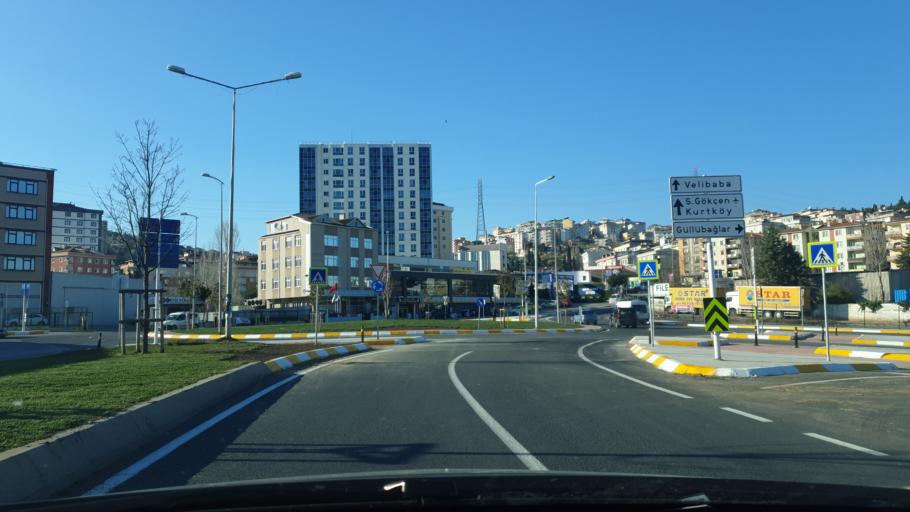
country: TR
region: Istanbul
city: Pendik
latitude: 40.8970
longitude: 29.2601
